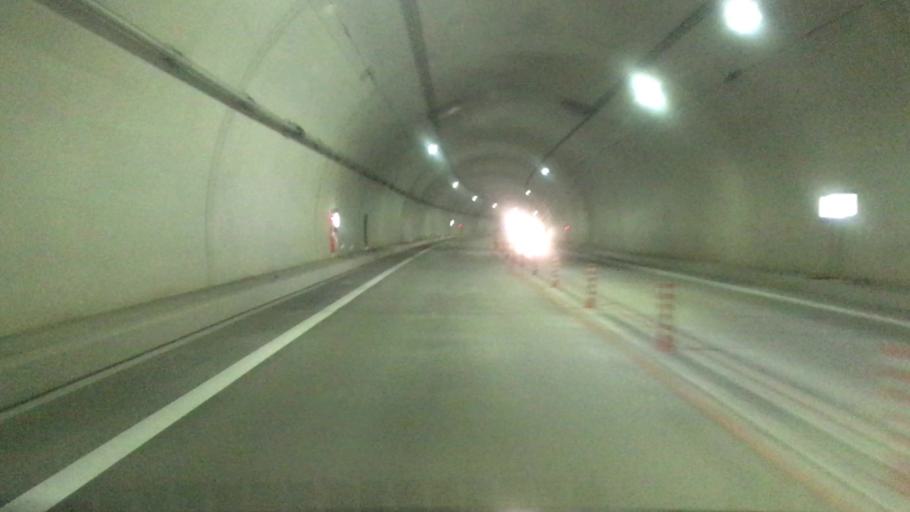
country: JP
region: Hyogo
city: Toyooka
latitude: 35.6271
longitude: 134.5216
